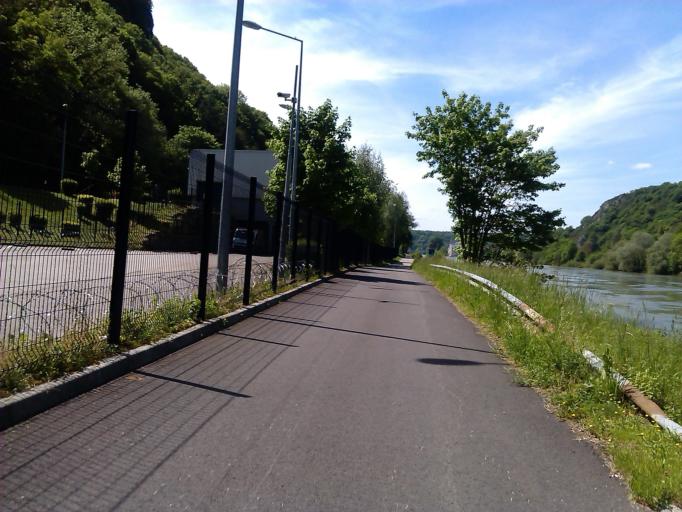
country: FR
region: Franche-Comte
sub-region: Departement du Doubs
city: Avanne-Aveney
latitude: 47.1988
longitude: 5.9798
